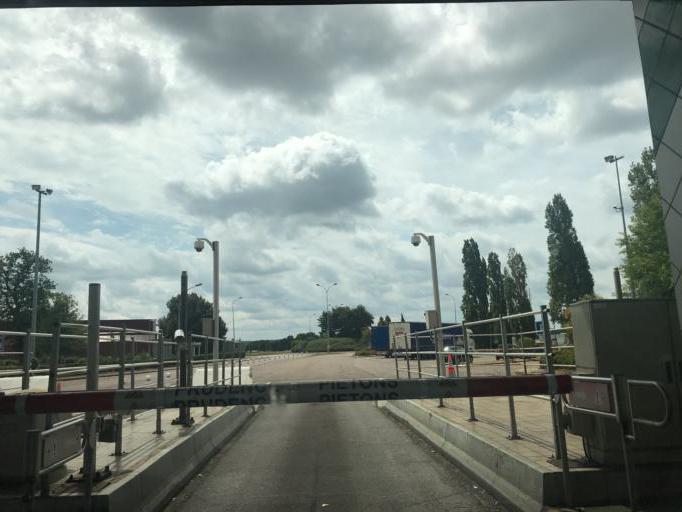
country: FR
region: Bourgogne
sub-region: Departement de l'Yonne
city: Avallon
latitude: 47.5093
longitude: 3.9920
